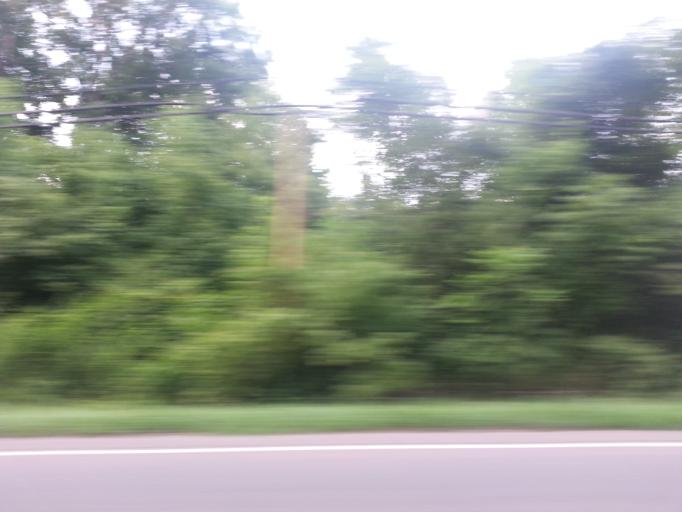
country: US
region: Tennessee
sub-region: Knox County
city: Knoxville
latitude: 36.1002
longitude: -83.9566
